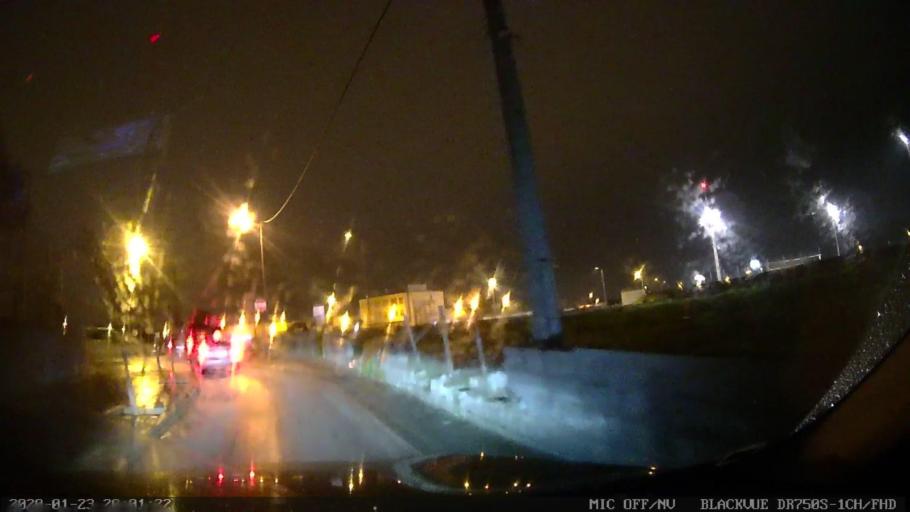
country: PT
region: Porto
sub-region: Matosinhos
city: Santa Cruz do Bispo
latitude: 41.2170
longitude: -8.6760
